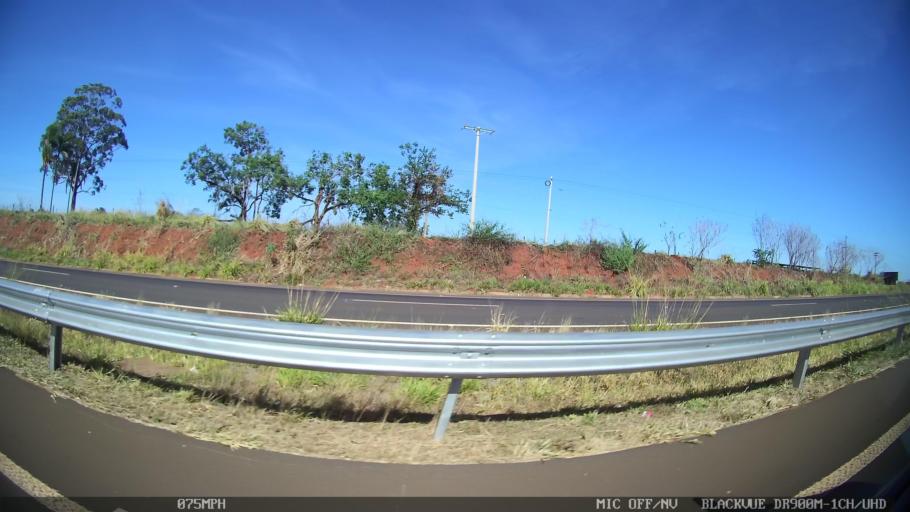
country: BR
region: Sao Paulo
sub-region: Barretos
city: Barretos
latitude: -20.5425
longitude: -48.6186
